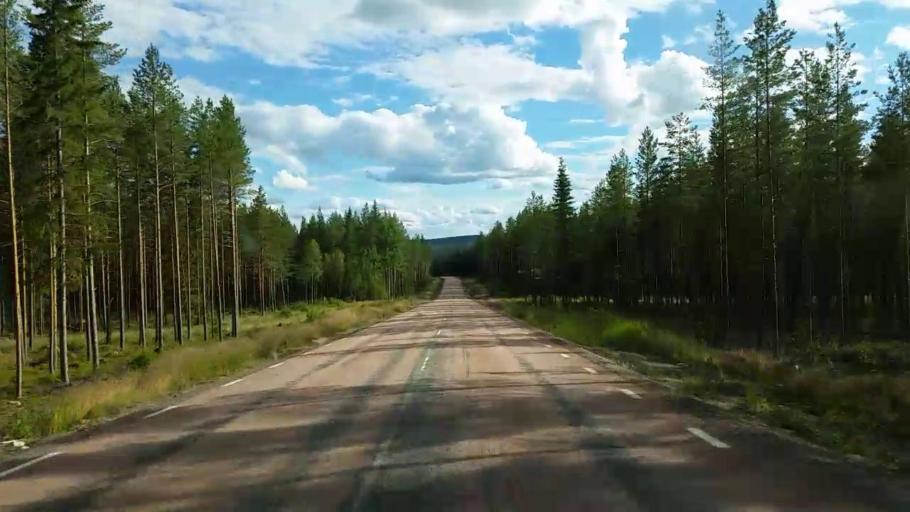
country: SE
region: Gaevleborg
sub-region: Ljusdals Kommun
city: Farila
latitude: 61.9441
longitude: 15.8828
